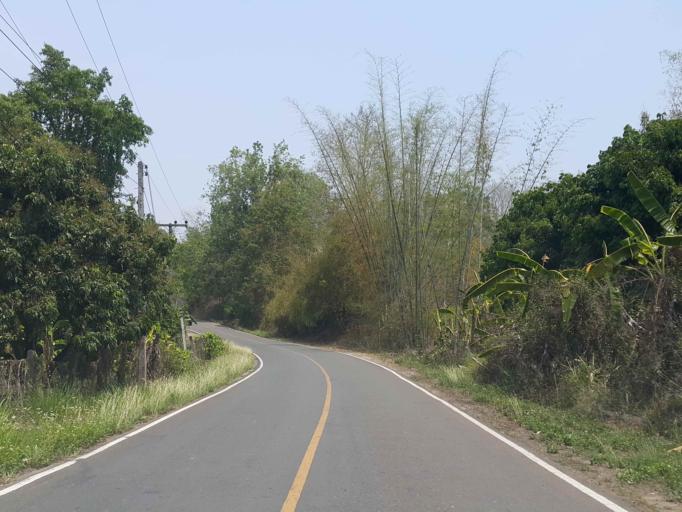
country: TH
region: Chiang Mai
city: Mae Taeng
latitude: 19.1262
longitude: 98.8851
